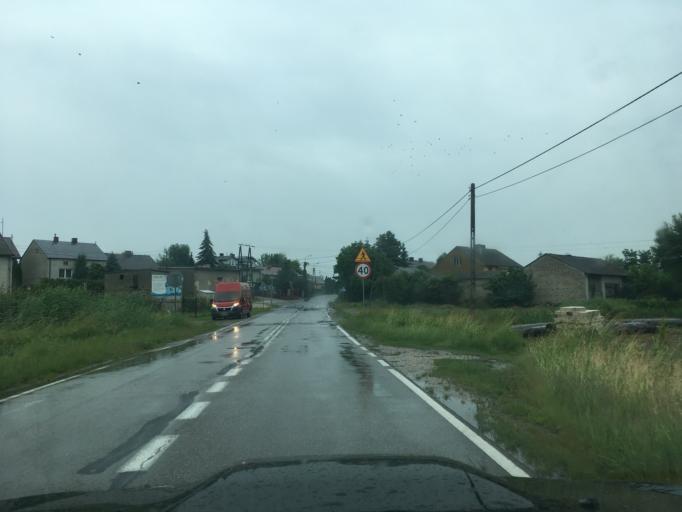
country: PL
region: Masovian Voivodeship
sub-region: Powiat otwocki
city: Sobienie Jeziory
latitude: 51.9808
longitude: 21.2829
